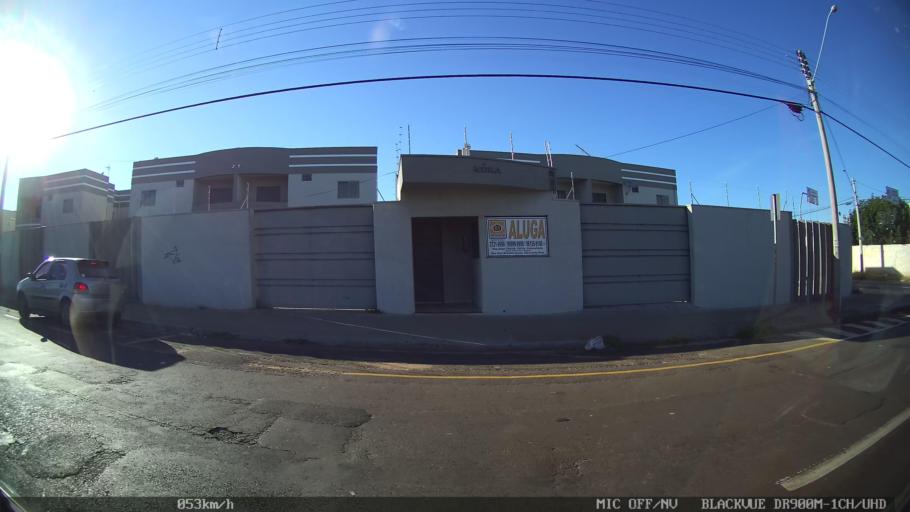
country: BR
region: Sao Paulo
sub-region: Franca
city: Franca
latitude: -20.5704
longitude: -47.4062
